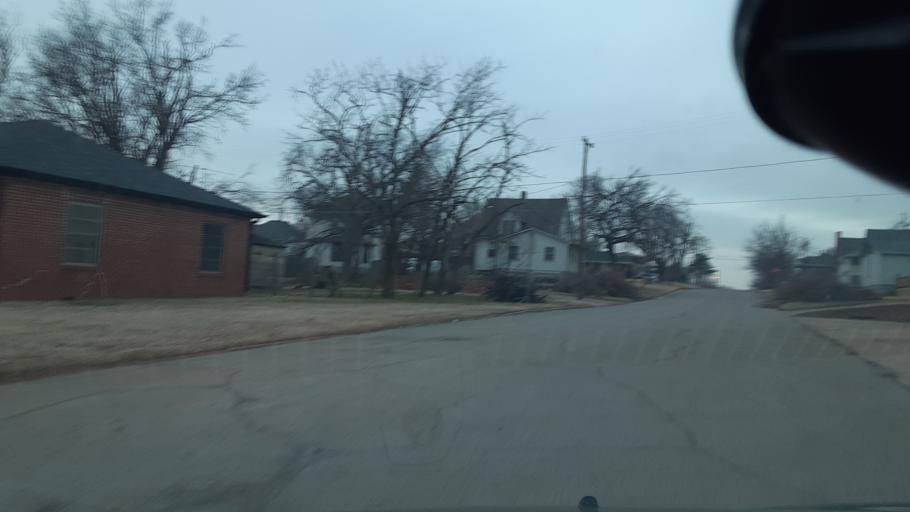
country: US
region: Oklahoma
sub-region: Logan County
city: Guthrie
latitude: 35.8782
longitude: -97.4163
